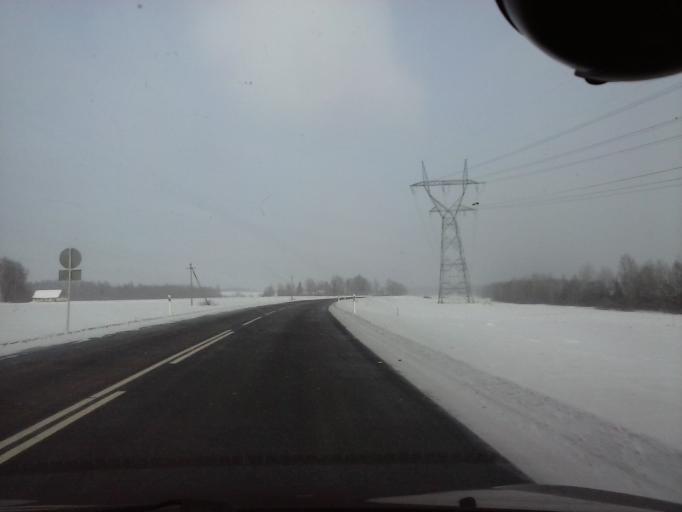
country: EE
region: Viljandimaa
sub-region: Abja vald
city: Abja-Paluoja
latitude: 58.2745
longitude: 25.2715
